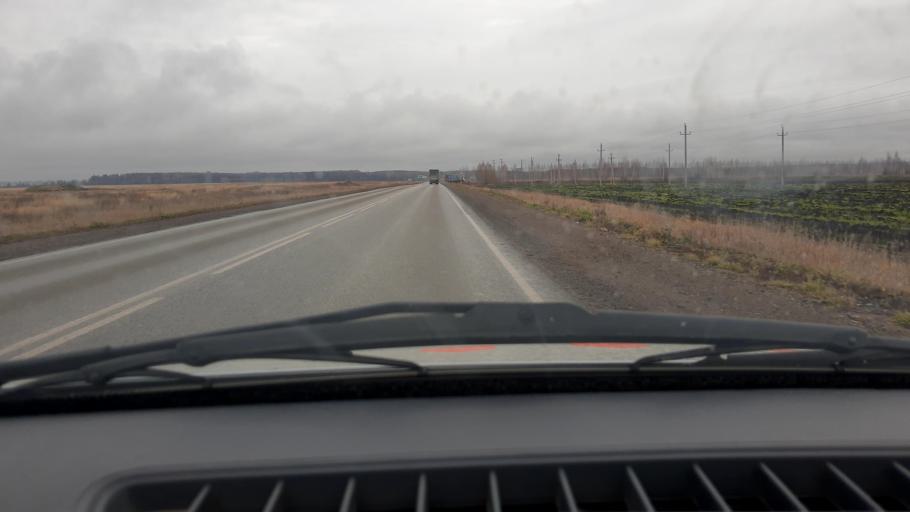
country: RU
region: Bashkortostan
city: Iglino
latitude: 54.7549
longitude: 56.2824
